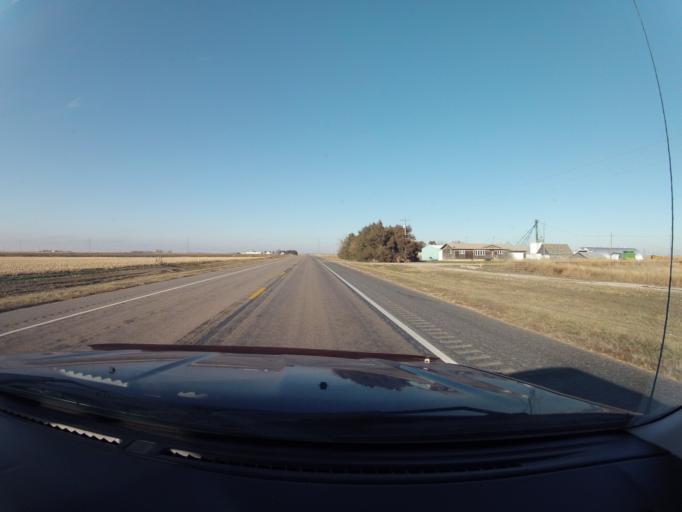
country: US
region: Nebraska
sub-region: Kearney County
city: Minden
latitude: 40.5363
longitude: -98.9518
